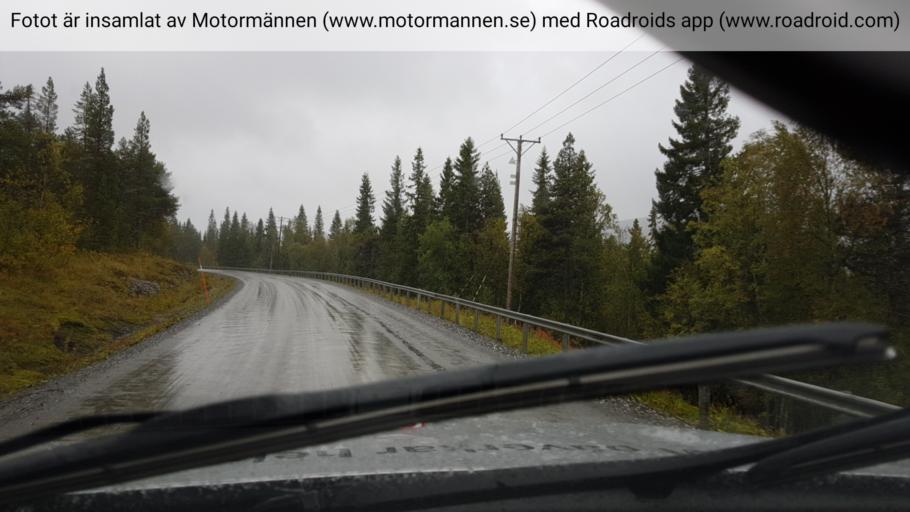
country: SE
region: Jaemtland
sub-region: Are Kommun
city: Are
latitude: 63.6804
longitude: 12.8115
